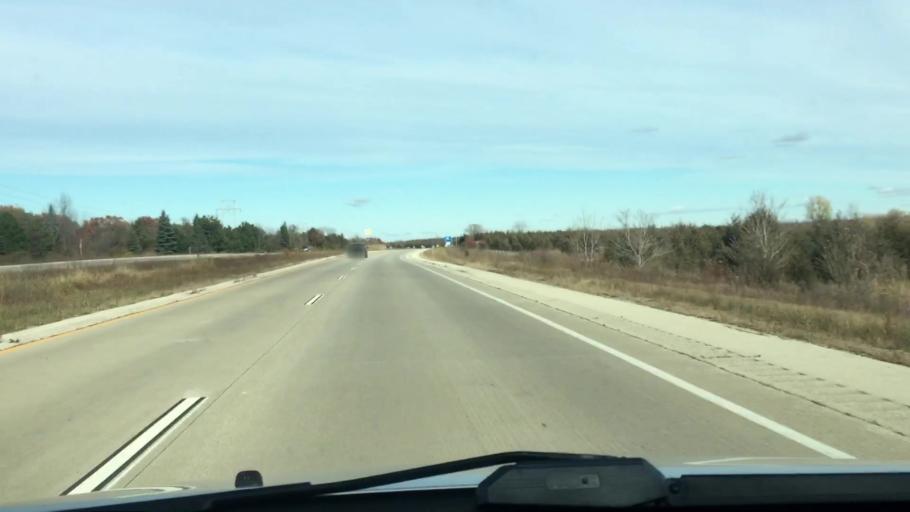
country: US
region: Wisconsin
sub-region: Kewaunee County
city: Luxemburg
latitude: 44.6148
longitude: -87.8322
